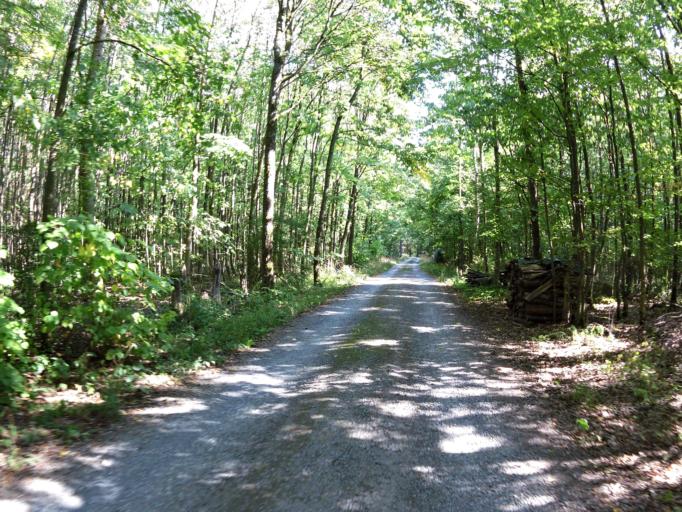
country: DE
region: Bavaria
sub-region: Regierungsbezirk Unterfranken
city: Margetshochheim
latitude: 49.8602
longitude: 9.8747
